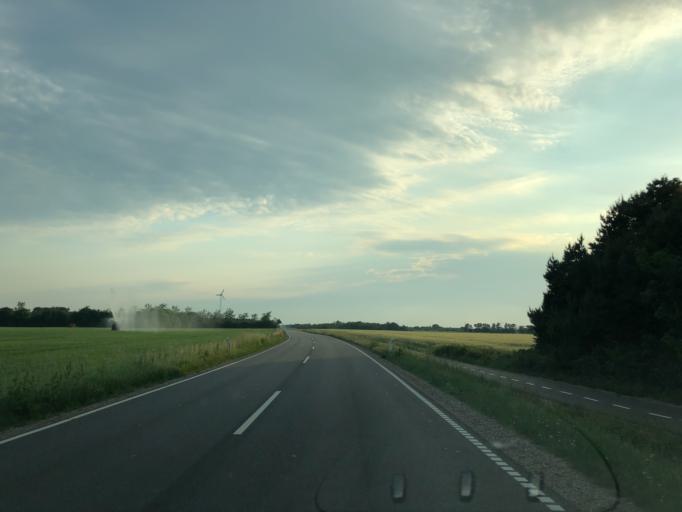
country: DK
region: Central Jutland
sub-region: Holstebro Kommune
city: Ulfborg
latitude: 56.3652
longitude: 8.4168
